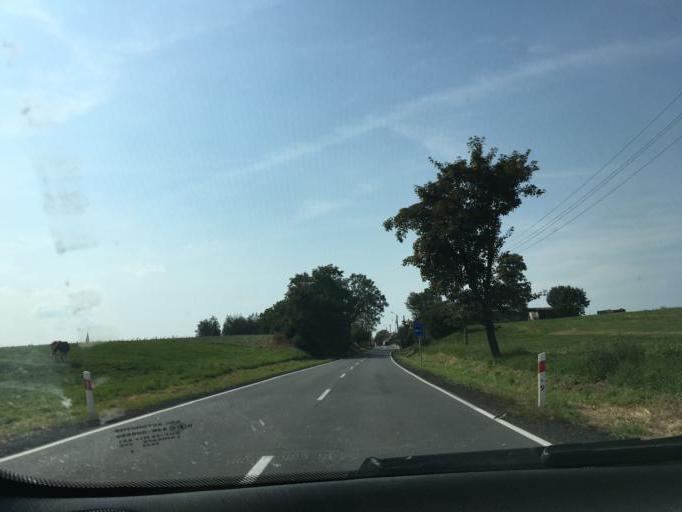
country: PL
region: Opole Voivodeship
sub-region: Powiat nyski
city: Nysa
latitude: 50.4235
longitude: 17.4392
